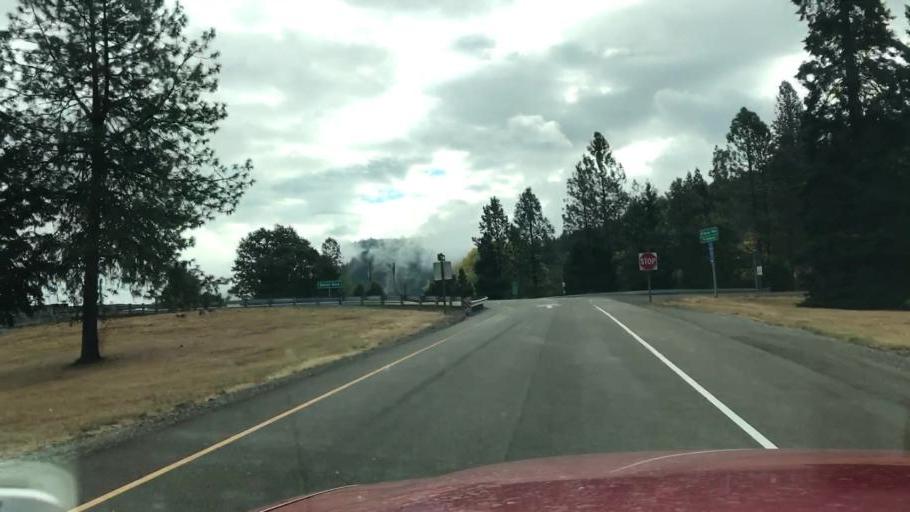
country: US
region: Oregon
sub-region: Douglas County
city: Canyonville
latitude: 42.7660
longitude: -123.3334
